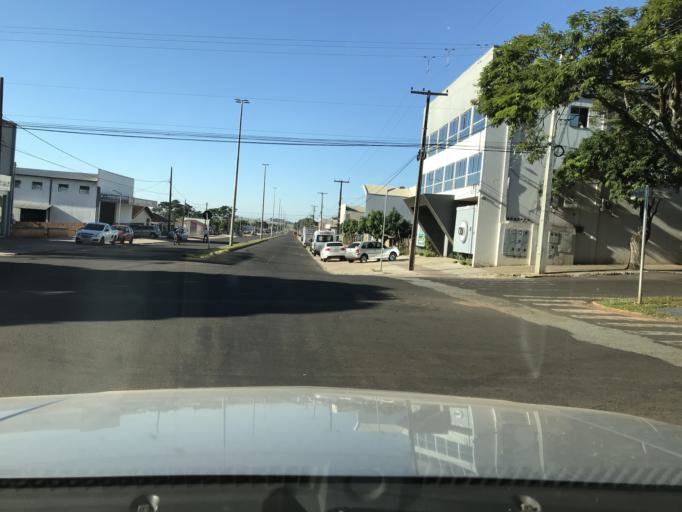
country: BR
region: Parana
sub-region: Ipora
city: Ipora
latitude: -23.9987
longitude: -53.7041
